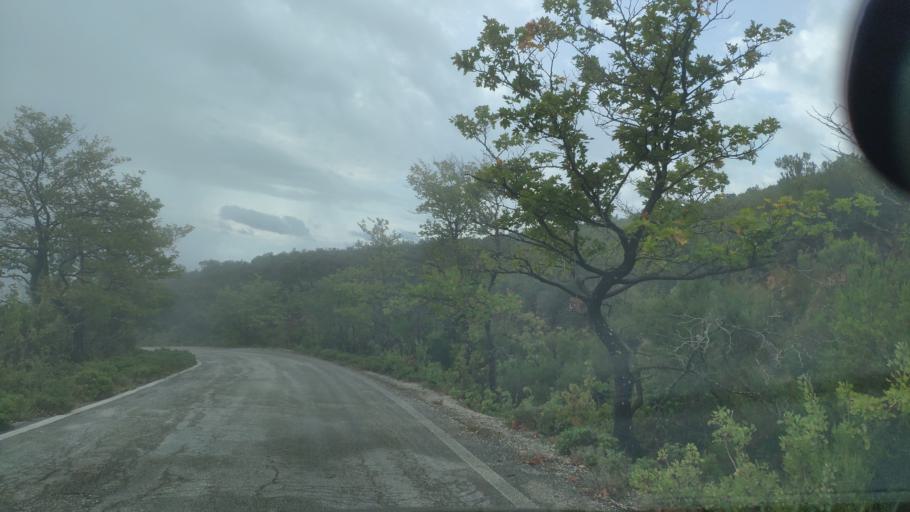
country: GR
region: West Greece
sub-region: Nomos Aitolias kai Akarnanias
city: Sardinia
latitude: 38.8482
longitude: 21.3159
